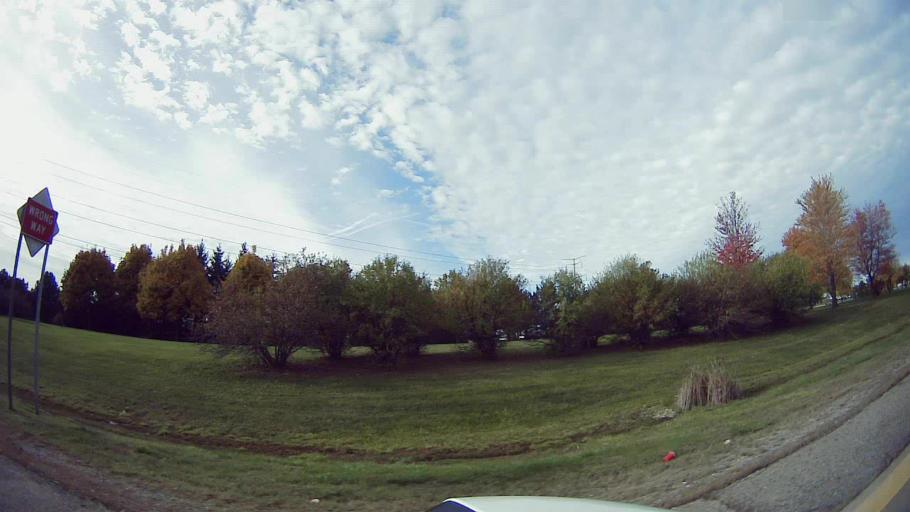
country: US
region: Michigan
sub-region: Oakland County
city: Novi
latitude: 42.4884
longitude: -83.4731
